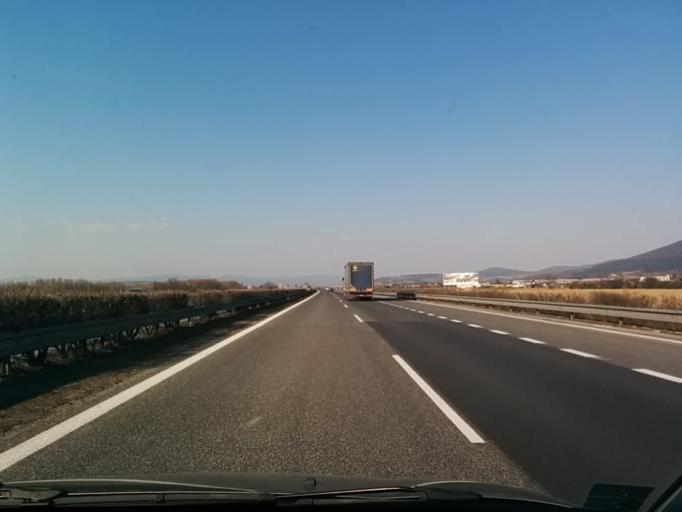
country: SK
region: Trenciansky
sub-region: Okres Nove Mesto nad Vahom
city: Nove Mesto nad Vahom
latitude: 48.7114
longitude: 17.8731
